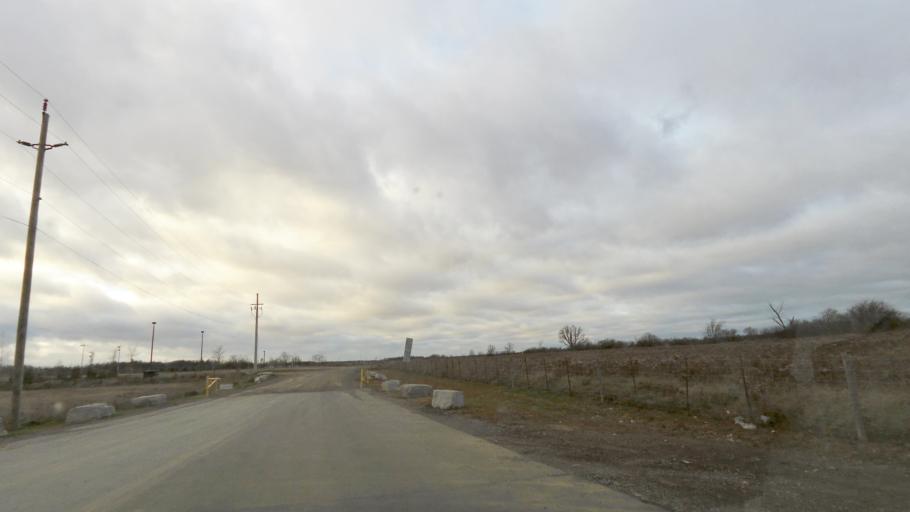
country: CA
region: Ontario
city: Burlington
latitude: 43.4412
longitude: -79.7716
